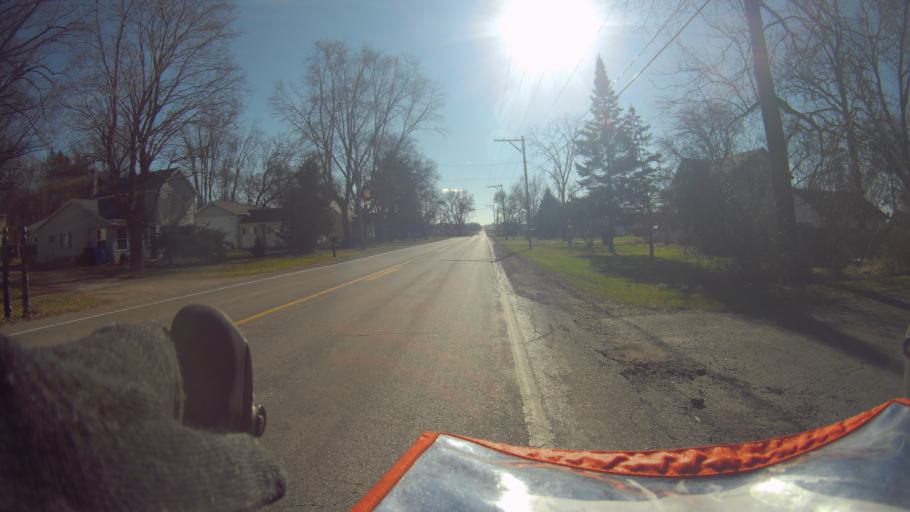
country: US
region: Wisconsin
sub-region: Green County
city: Brooklyn
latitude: 42.8494
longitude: -89.3692
